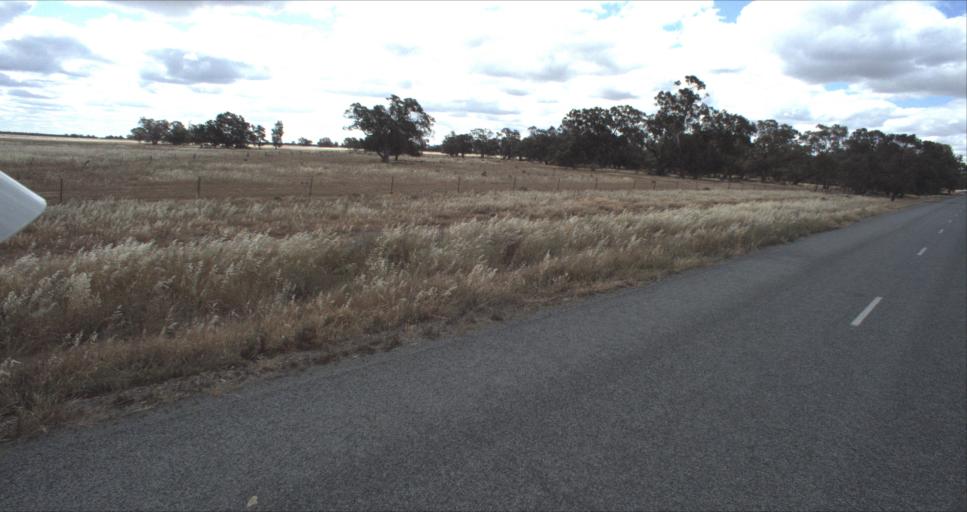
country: AU
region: New South Wales
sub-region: Leeton
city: Leeton
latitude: -34.6938
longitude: 146.3432
